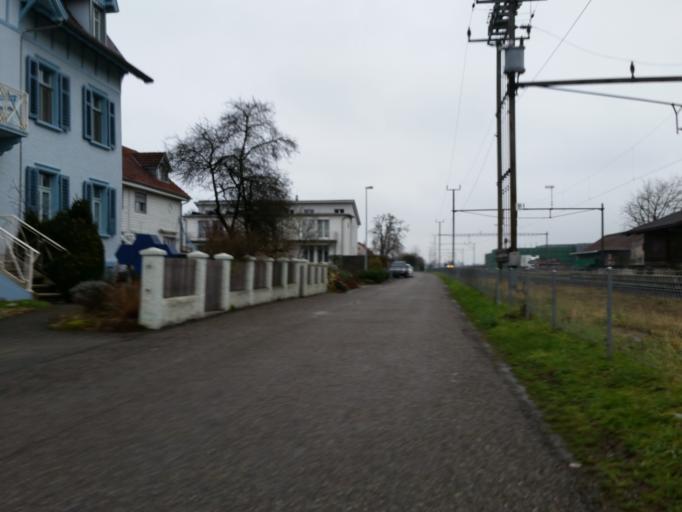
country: CH
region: Thurgau
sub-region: Arbon District
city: Egnach
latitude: 47.5444
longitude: 9.3827
